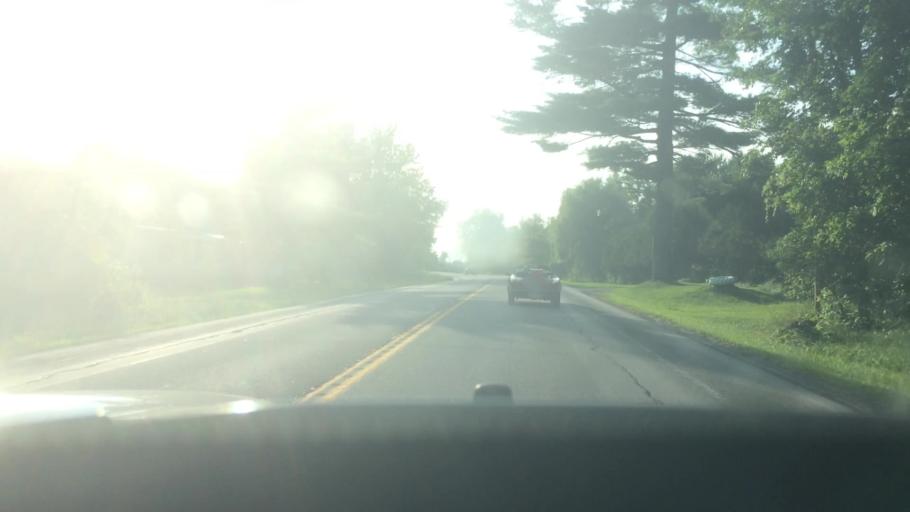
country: US
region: New York
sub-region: St. Lawrence County
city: Canton
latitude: 44.6493
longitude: -75.2929
